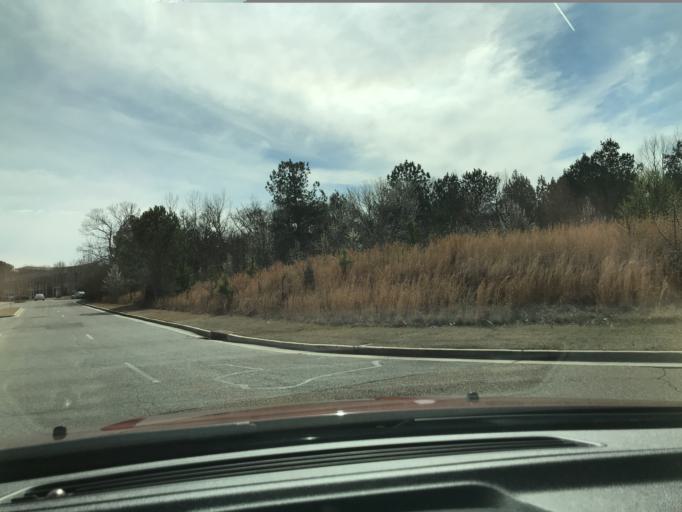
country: US
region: Tennessee
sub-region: Shelby County
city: Collierville
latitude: 35.0410
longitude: -89.7208
